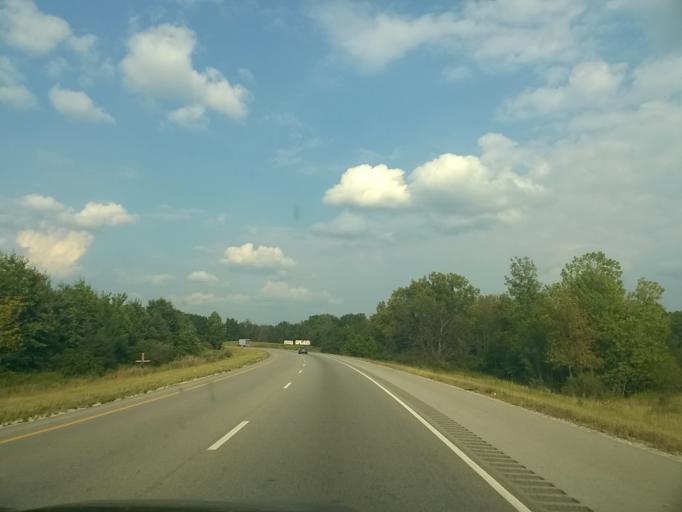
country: US
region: Indiana
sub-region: Vigo County
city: Seelyville
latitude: 39.4460
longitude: -87.2069
